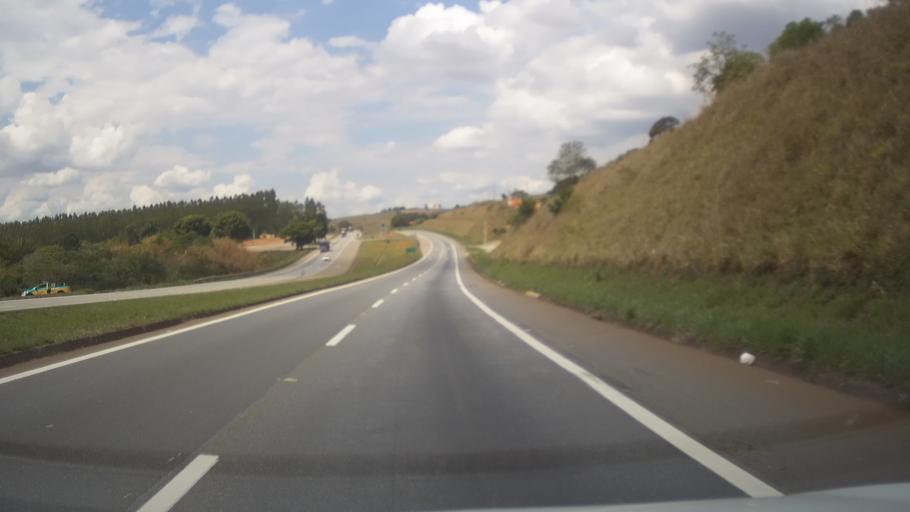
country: BR
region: Minas Gerais
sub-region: Nepomuceno
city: Nepomuceno
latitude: -21.3072
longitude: -45.1592
